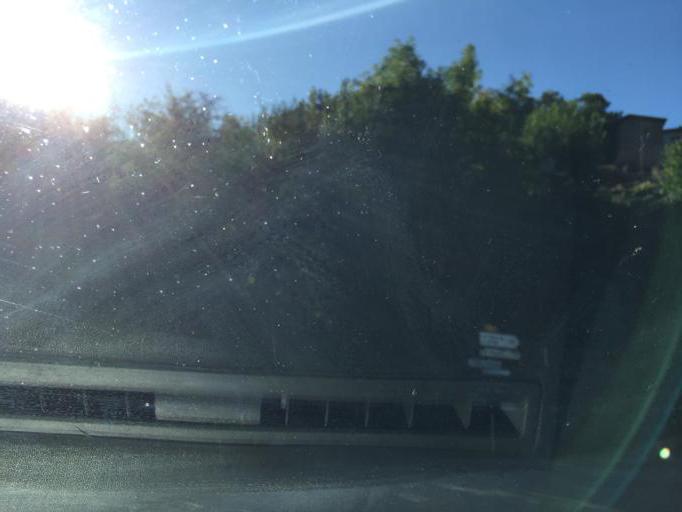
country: FR
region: Rhone-Alpes
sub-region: Departement de la Loire
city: Saint-Paul-en-Jarez
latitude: 45.4277
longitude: 4.5838
